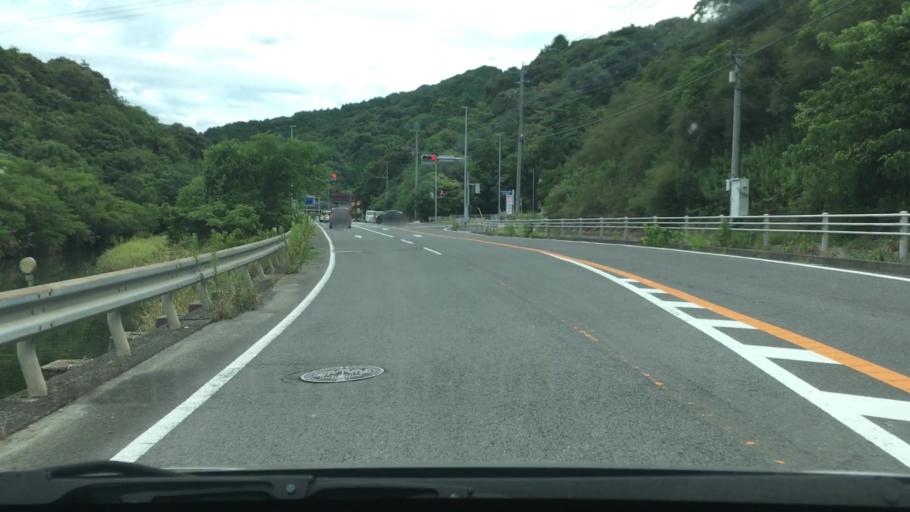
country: JP
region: Nagasaki
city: Sasebo
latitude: 32.9972
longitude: 129.7322
